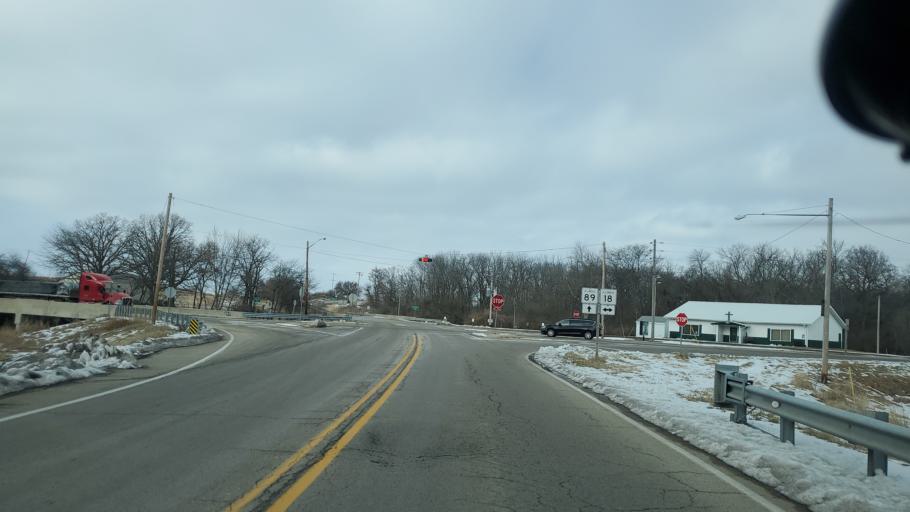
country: US
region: Illinois
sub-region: Marshall County
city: Toluca
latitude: 41.1180
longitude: -89.2016
